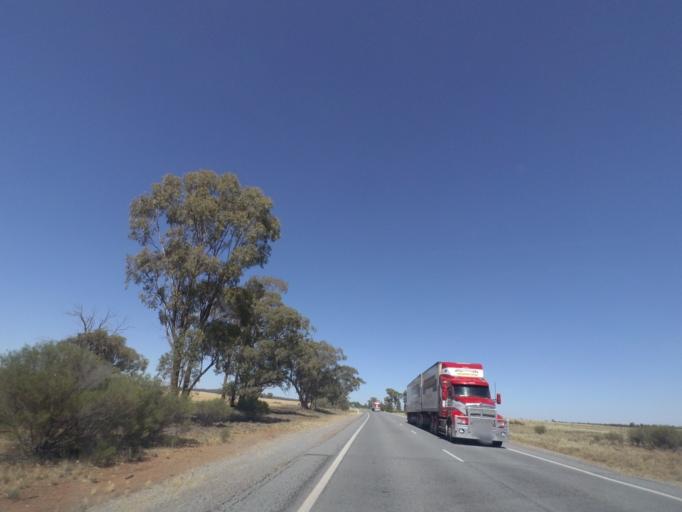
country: AU
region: New South Wales
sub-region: Narrandera
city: Narrandera
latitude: -34.4123
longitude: 146.8725
